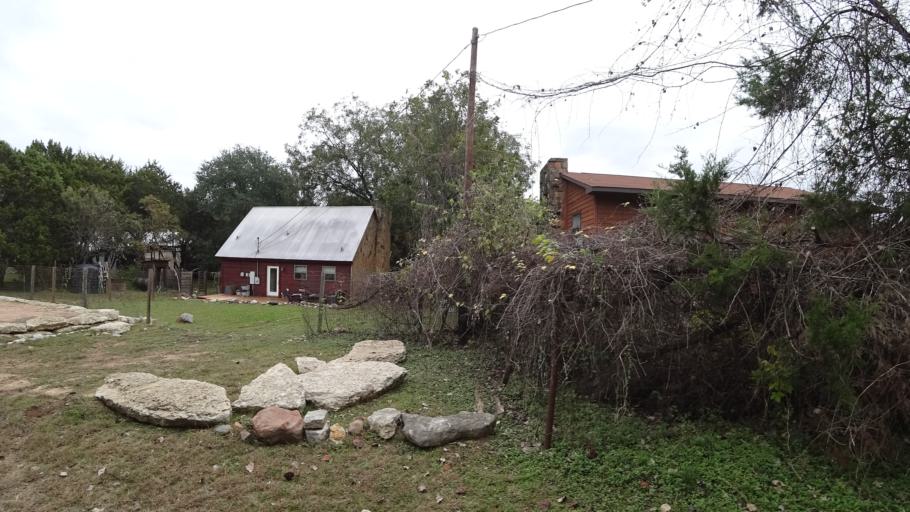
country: US
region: Texas
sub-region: Travis County
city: Bee Cave
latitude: 30.3537
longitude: -97.9205
